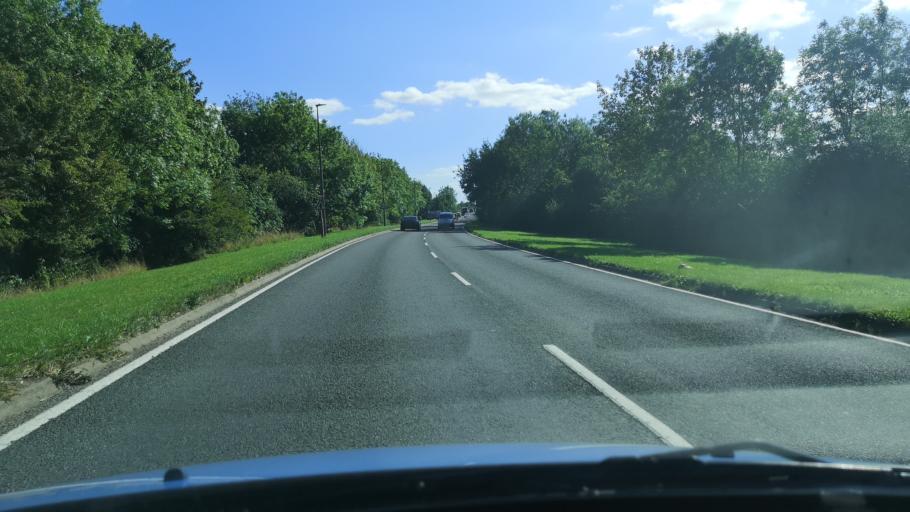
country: GB
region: England
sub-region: North Lincolnshire
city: Crowle
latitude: 53.5938
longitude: -0.8191
